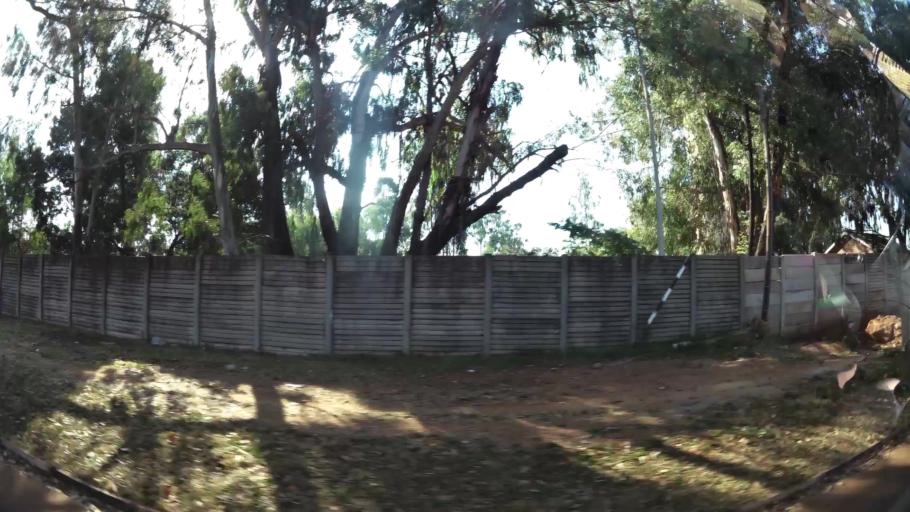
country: ZA
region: Gauteng
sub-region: West Rand District Municipality
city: Randfontein
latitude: -26.1657
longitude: 27.7027
